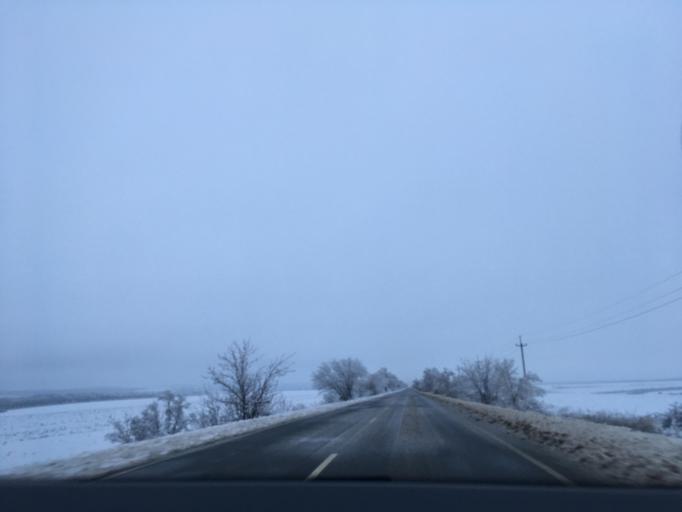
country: RU
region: Voronezj
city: Verkhniy Mamon
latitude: 50.0222
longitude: 40.0912
